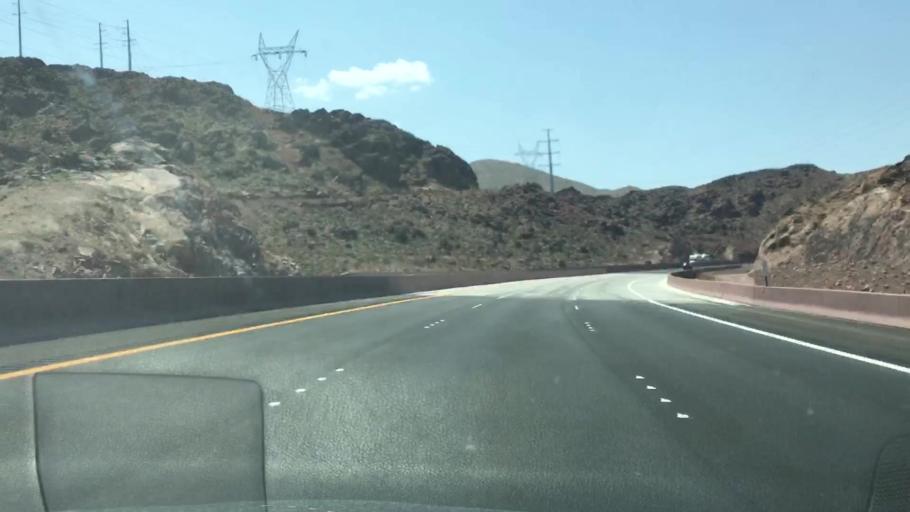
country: US
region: Nevada
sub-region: Clark County
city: Boulder City
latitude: 36.0054
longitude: -114.7821
